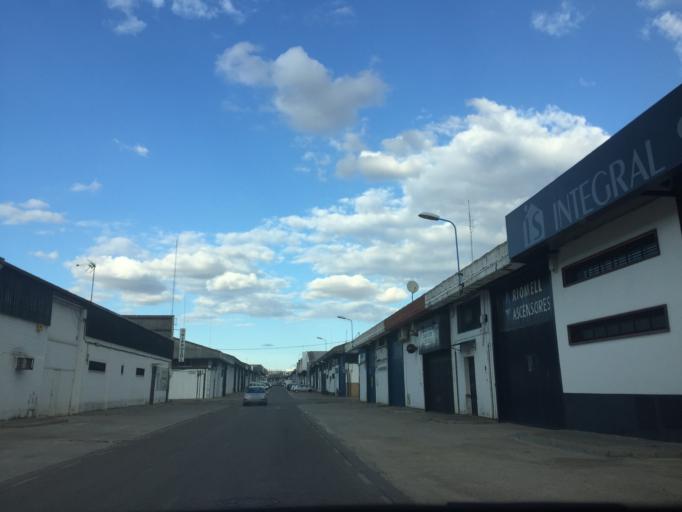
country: ES
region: Andalusia
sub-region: Provincia de Sevilla
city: Sevilla
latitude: 37.3643
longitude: -5.9604
